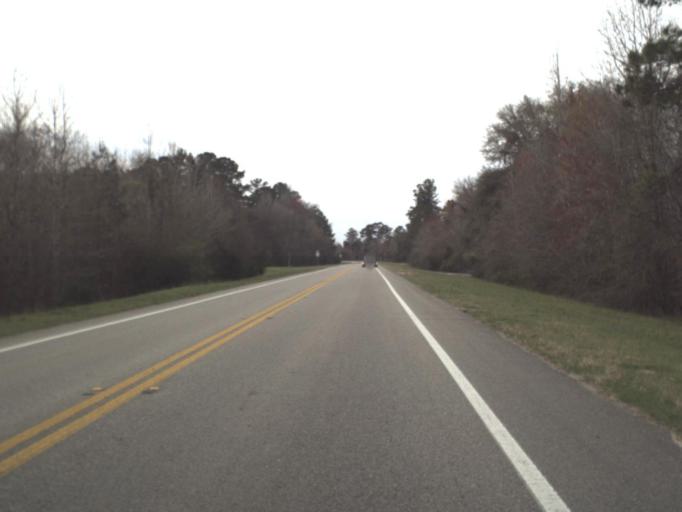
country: US
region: Florida
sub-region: Gadsden County
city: Quincy
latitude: 30.3859
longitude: -84.6555
